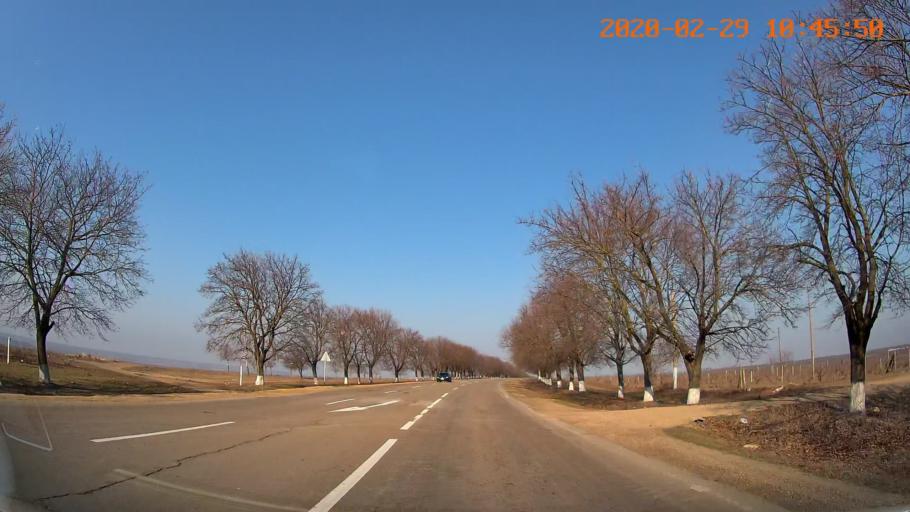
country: MD
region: Telenesti
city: Grigoriopol
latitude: 47.0791
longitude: 29.3789
